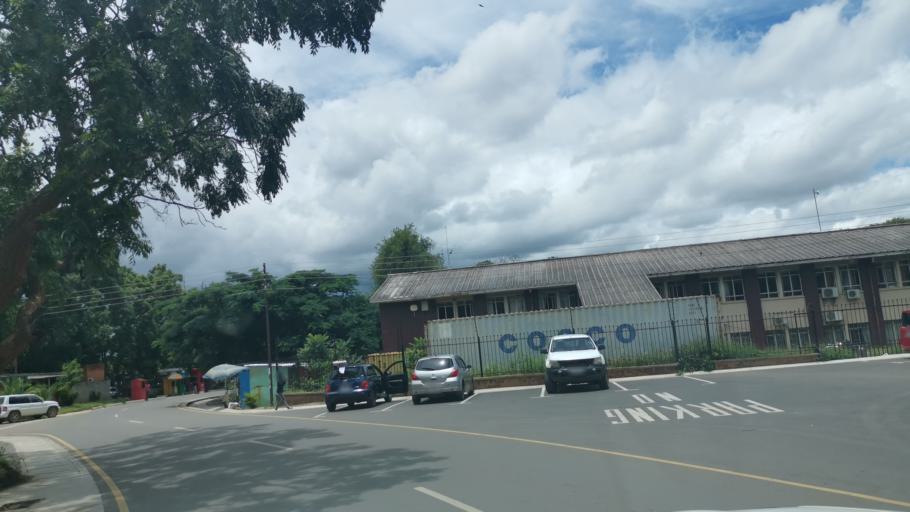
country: ZM
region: Lusaka
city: Lusaka
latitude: -15.4250
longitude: 28.3096
